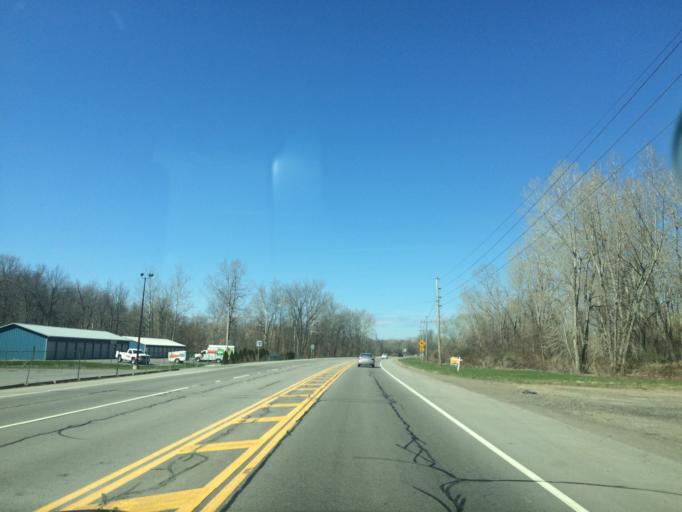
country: US
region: New York
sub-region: Wayne County
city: Palmyra
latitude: 43.0618
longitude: -77.2575
